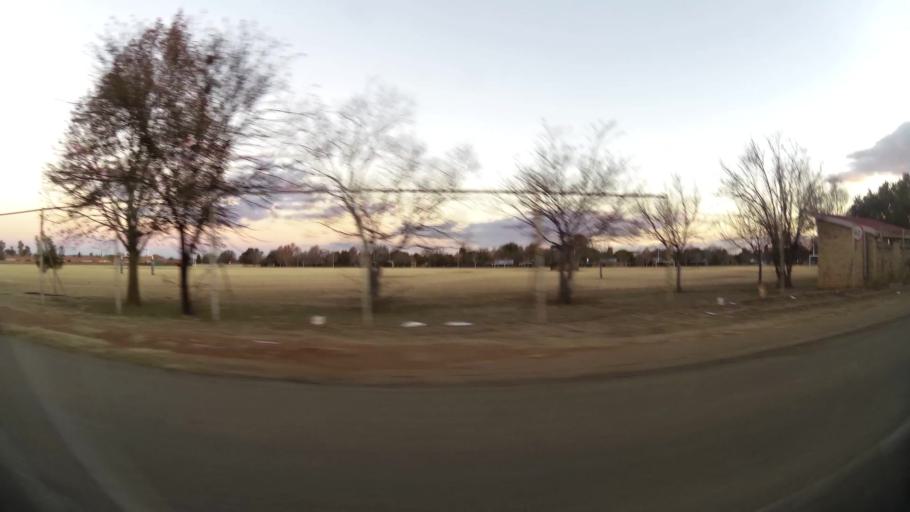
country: ZA
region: North-West
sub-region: Dr Kenneth Kaunda District Municipality
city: Potchefstroom
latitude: -26.7086
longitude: 27.1180
